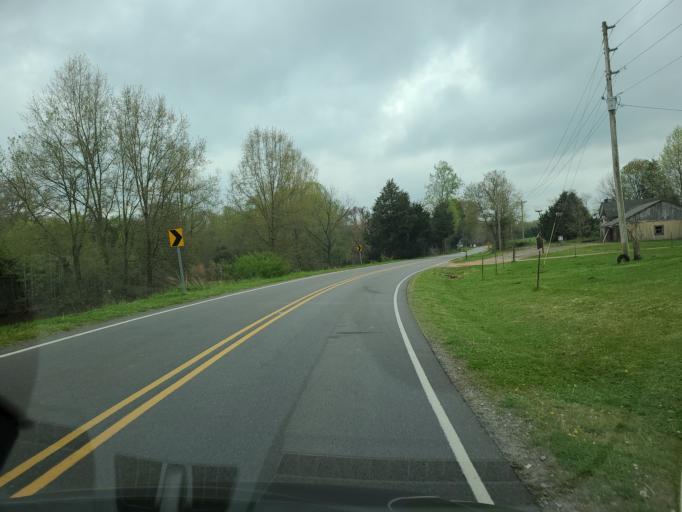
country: US
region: North Carolina
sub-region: Gaston County
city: Cherryville
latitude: 35.4446
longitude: -81.3722
